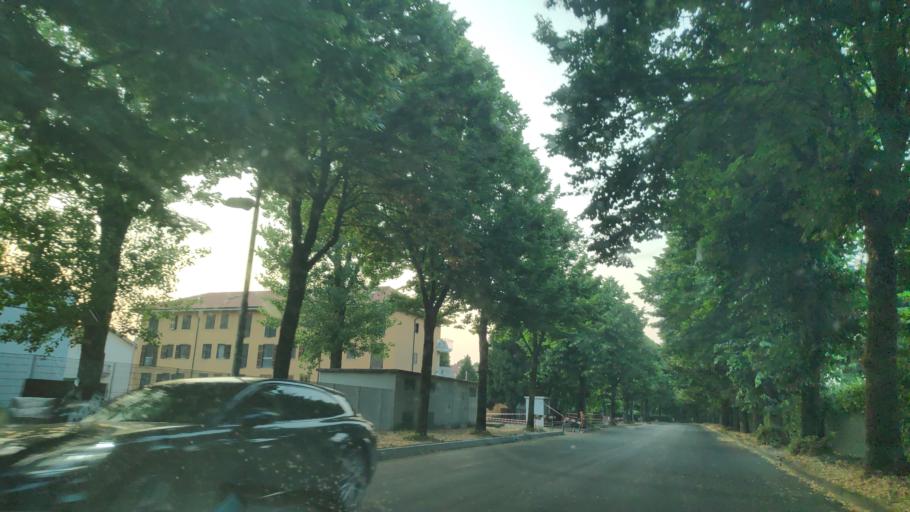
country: IT
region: Lombardy
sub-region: Citta metropolitana di Milano
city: Paullo
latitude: 45.4208
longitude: 9.4085
